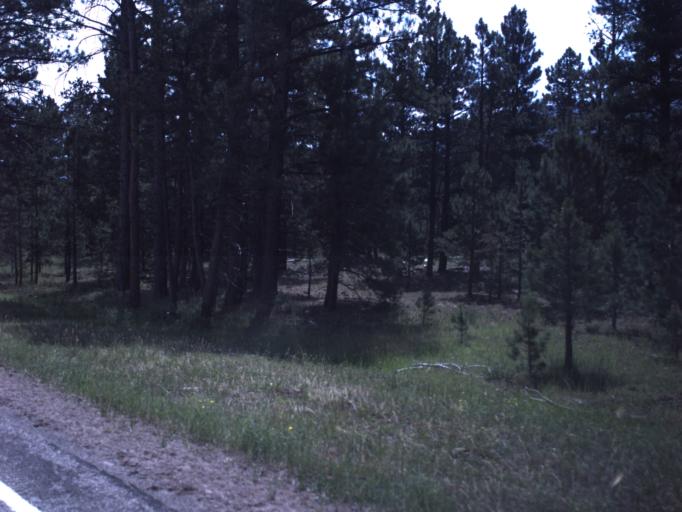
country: US
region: Utah
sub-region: Daggett County
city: Manila
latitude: 40.8526
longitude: -109.6019
